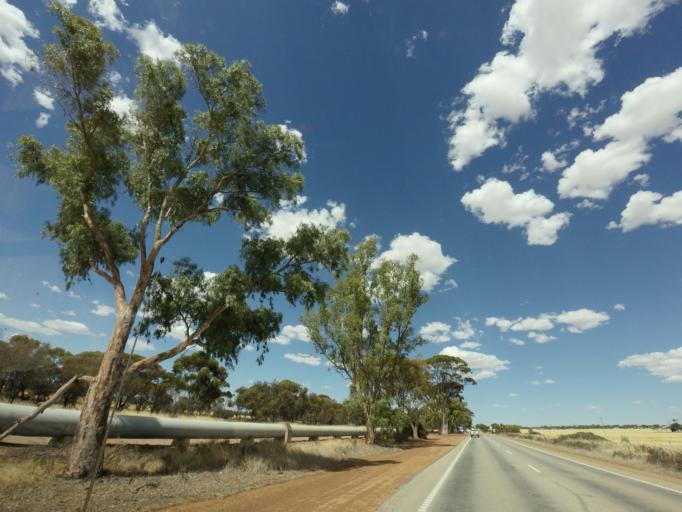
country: AU
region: Western Australia
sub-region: Cunderdin
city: Cunderdin
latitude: -31.6517
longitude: 117.2157
